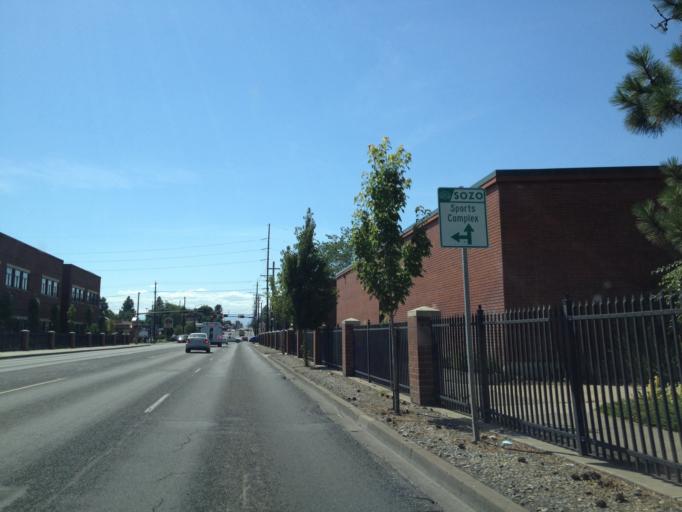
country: US
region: Washington
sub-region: Yakima County
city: Yakima
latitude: 46.5853
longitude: -120.5283
